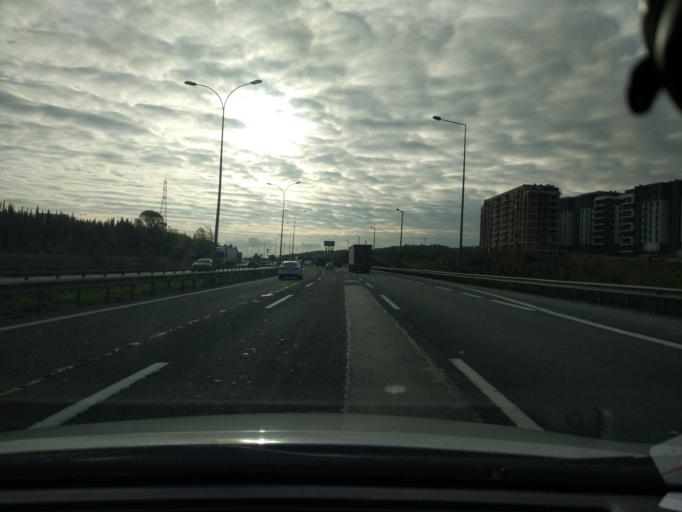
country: TR
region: Kocaeli
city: Balcik
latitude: 40.8392
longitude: 29.4162
